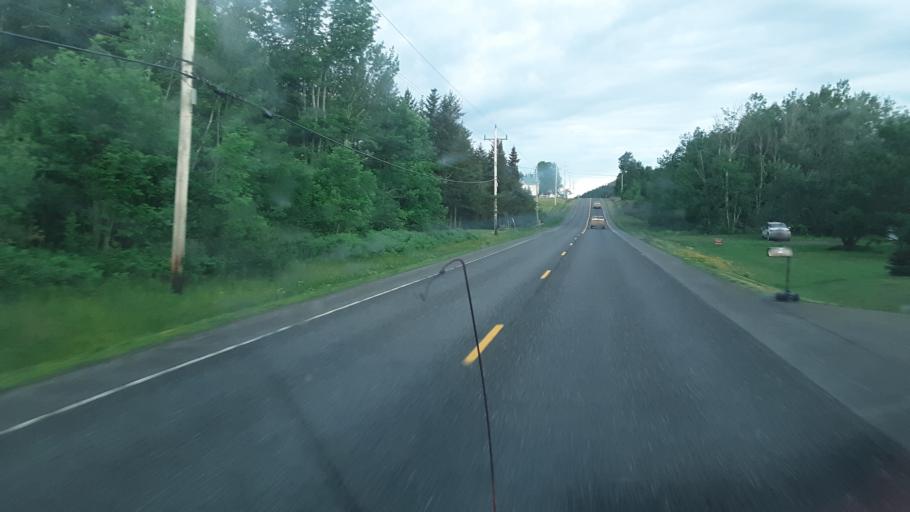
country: US
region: Maine
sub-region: Aroostook County
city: Presque Isle
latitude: 46.6668
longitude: -68.2068
